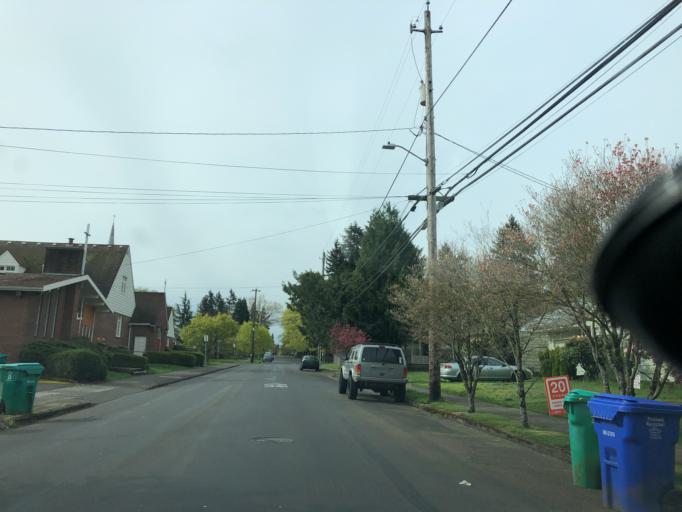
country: US
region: Oregon
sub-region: Multnomah County
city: Portland
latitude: 45.5545
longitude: -122.6255
